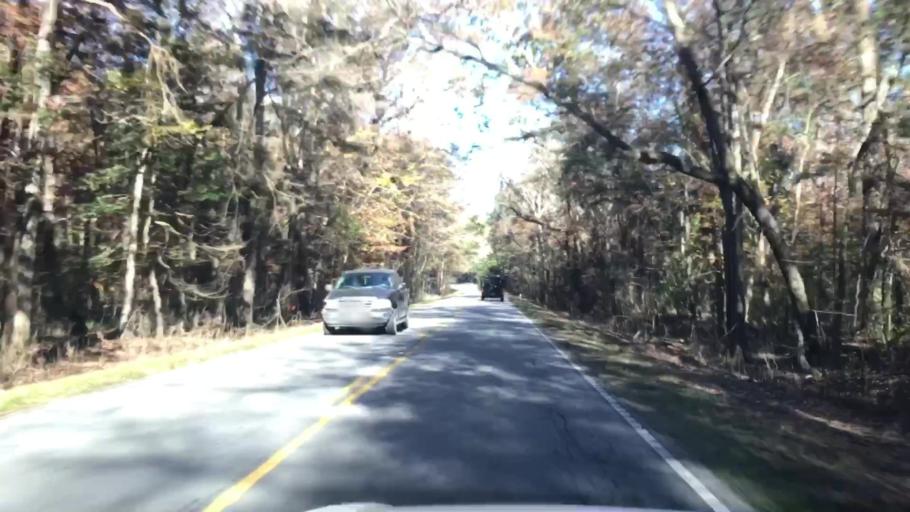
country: US
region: South Carolina
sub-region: Berkeley County
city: Ladson
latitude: 32.9076
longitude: -80.1480
